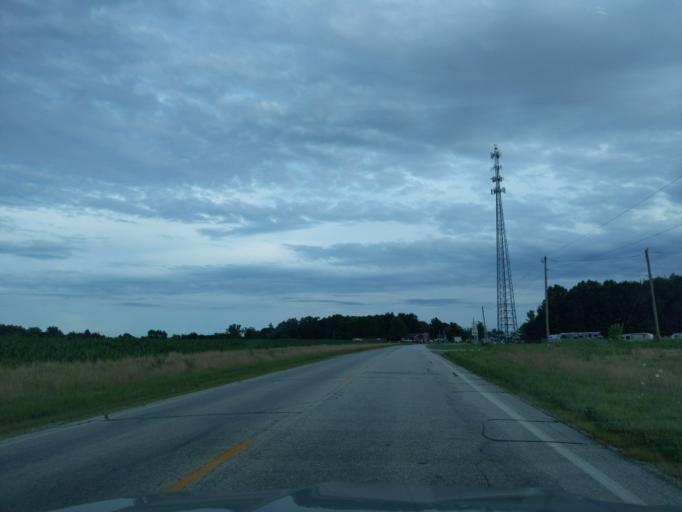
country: US
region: Indiana
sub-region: Ripley County
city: Sunman
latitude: 39.2756
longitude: -85.0984
